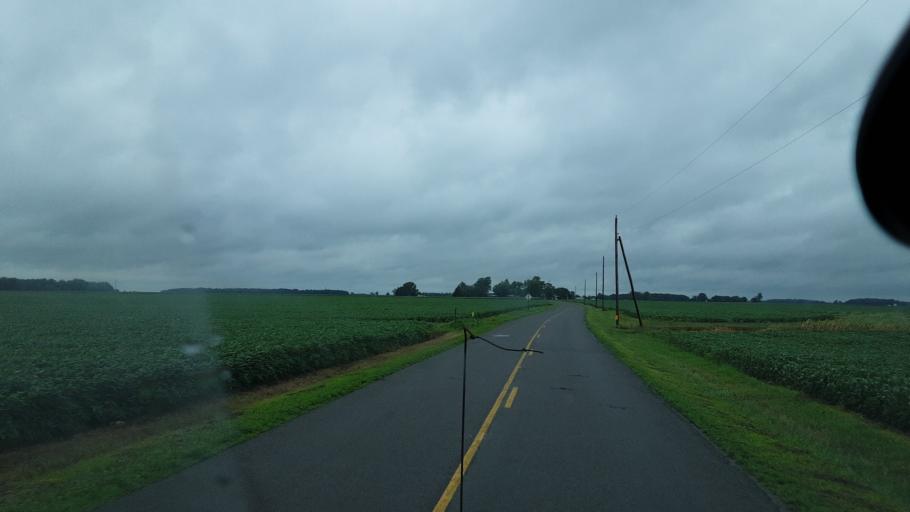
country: US
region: Ohio
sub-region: Van Wert County
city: Convoy
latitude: 40.8172
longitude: -84.6782
